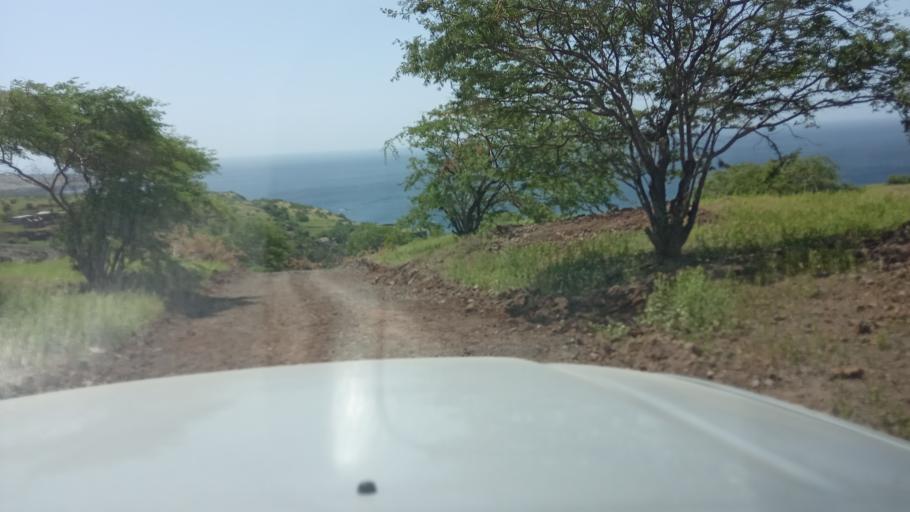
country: CV
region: Santa Catarina
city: Assomada
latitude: 15.1194
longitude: -23.7641
